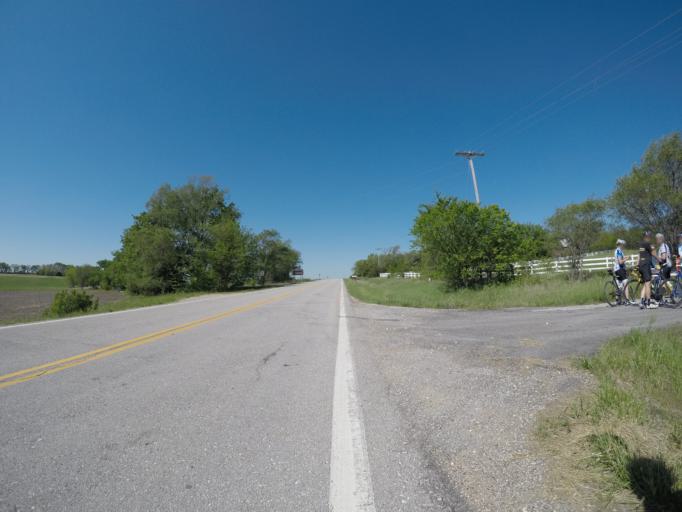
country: US
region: Kansas
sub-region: Osage County
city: Overbrook
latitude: 38.8887
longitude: -95.4276
